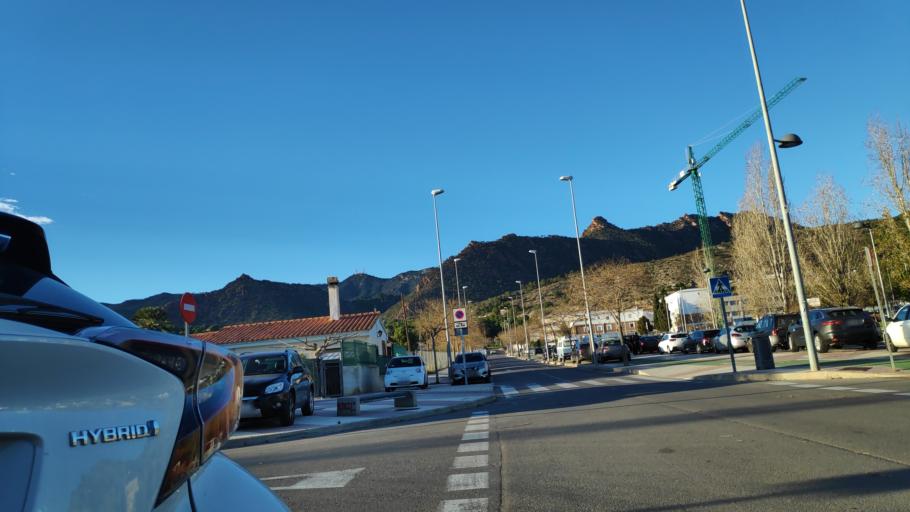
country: ES
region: Valencia
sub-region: Provincia de Castello
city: Benicassim
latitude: 40.0559
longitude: 0.0612
